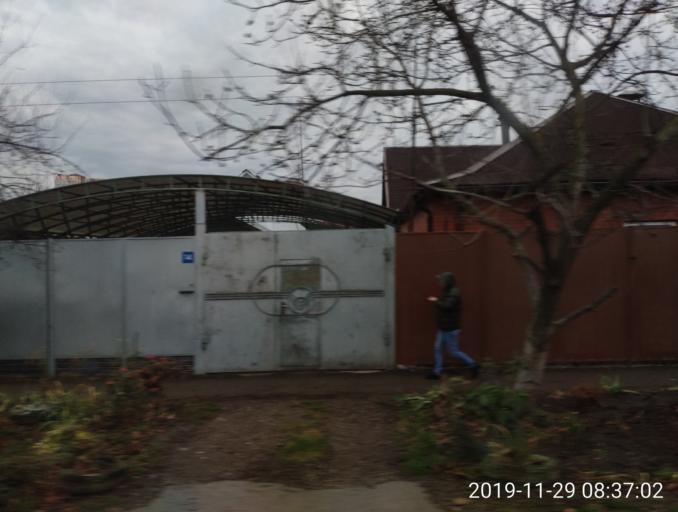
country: RU
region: Krasnodarskiy
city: Krasnodar
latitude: 45.0526
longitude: 39.0028
